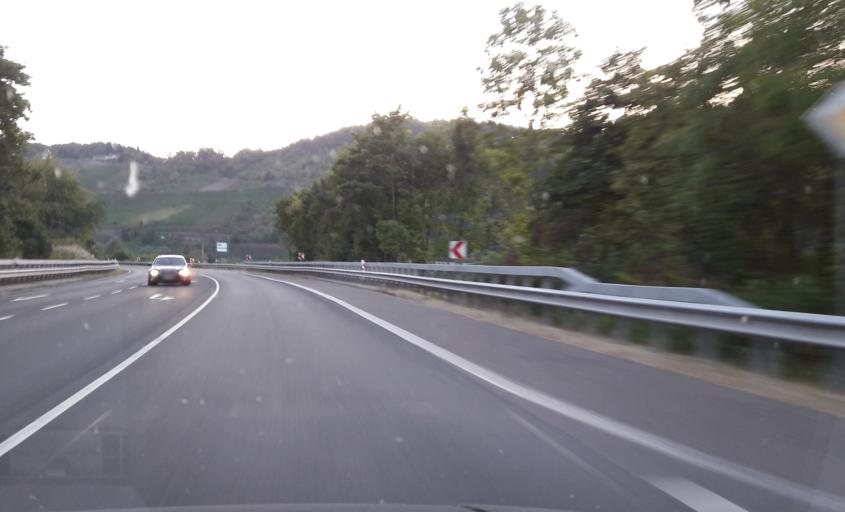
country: DE
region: Rheinland-Pfalz
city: Punderich
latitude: 50.0374
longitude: 7.1218
